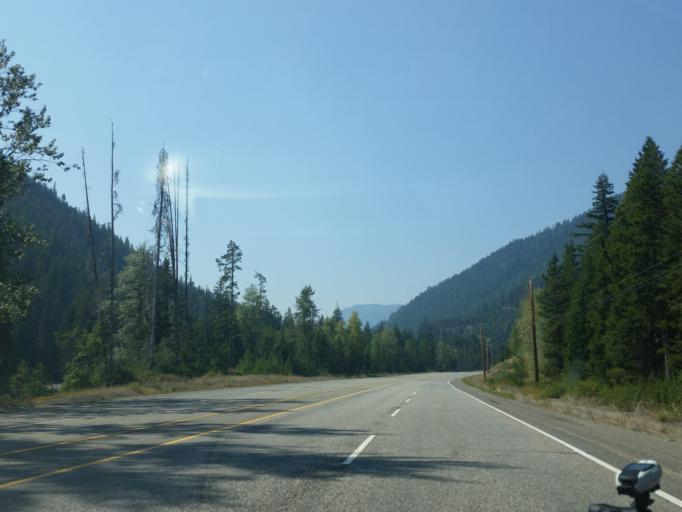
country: CA
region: British Columbia
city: Princeton
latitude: 49.0924
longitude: -120.6789
